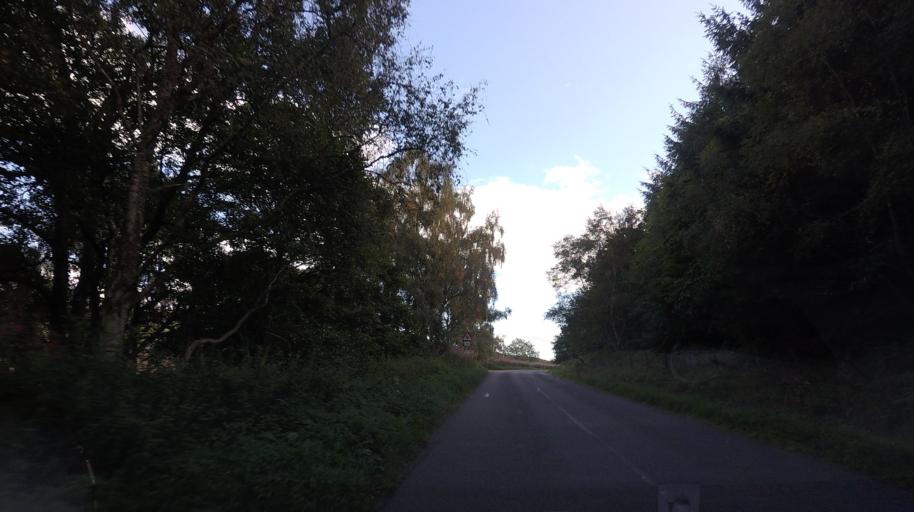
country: GB
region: Scotland
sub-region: Aberdeenshire
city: Torphins
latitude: 57.1249
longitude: -2.6720
